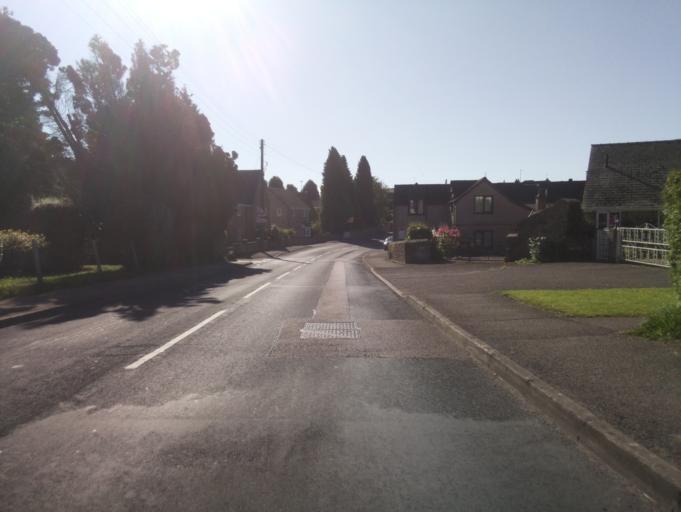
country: GB
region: England
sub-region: Gloucestershire
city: Coleford
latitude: 51.8120
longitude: -2.6180
